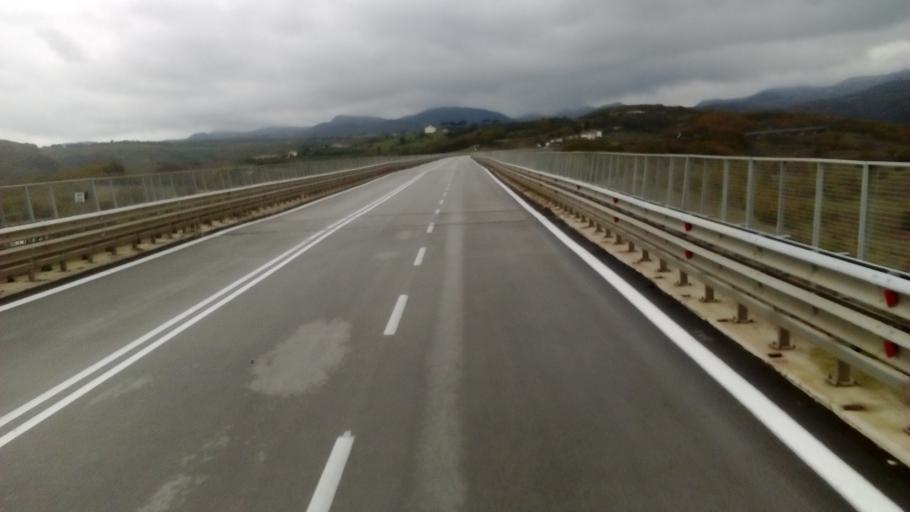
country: IT
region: Molise
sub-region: Provincia di Isernia
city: Bagnoli del Trigno
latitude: 41.7276
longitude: 14.4562
